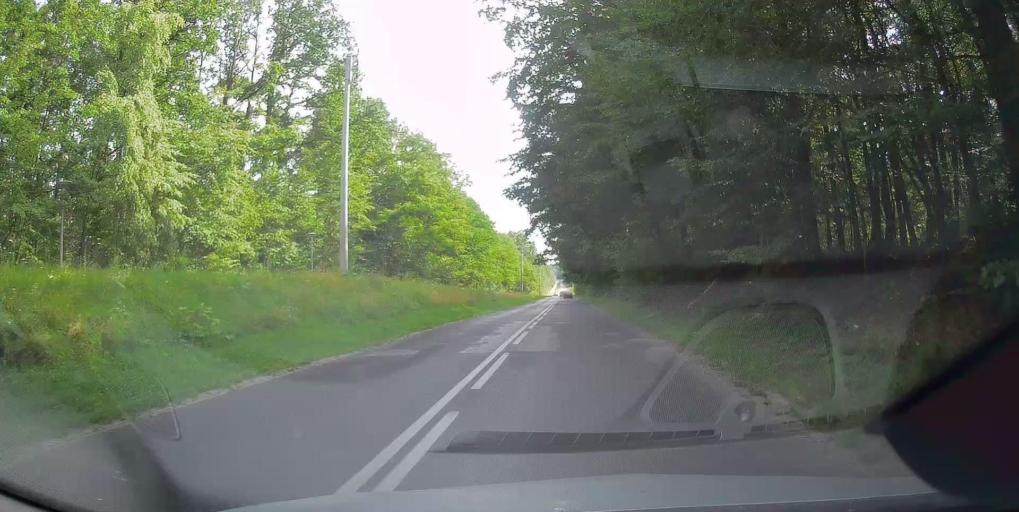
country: PL
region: Lodz Voivodeship
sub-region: Powiat tomaszowski
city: Tomaszow Mazowiecki
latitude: 51.5127
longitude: 20.0000
